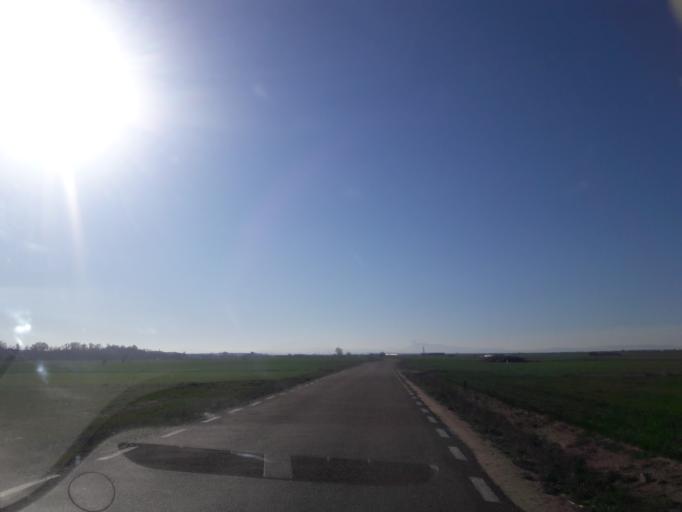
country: ES
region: Castille and Leon
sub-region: Provincia de Salamanca
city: Coca de Alba
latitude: 40.8669
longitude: -5.3730
